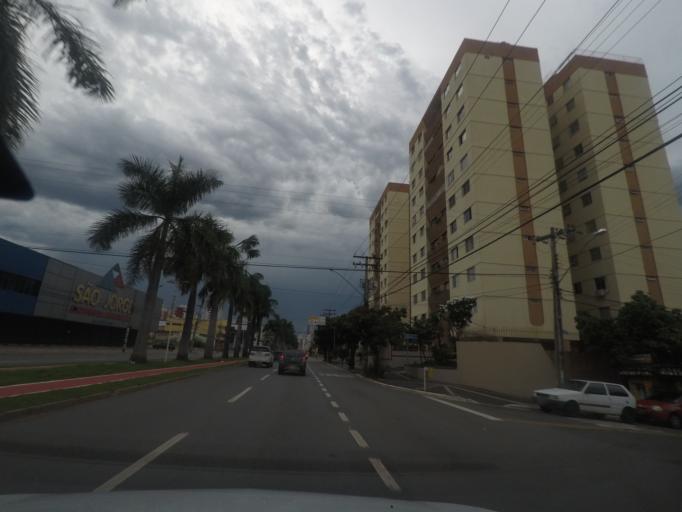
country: BR
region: Goias
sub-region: Goiania
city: Goiania
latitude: -16.7138
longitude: -49.2555
